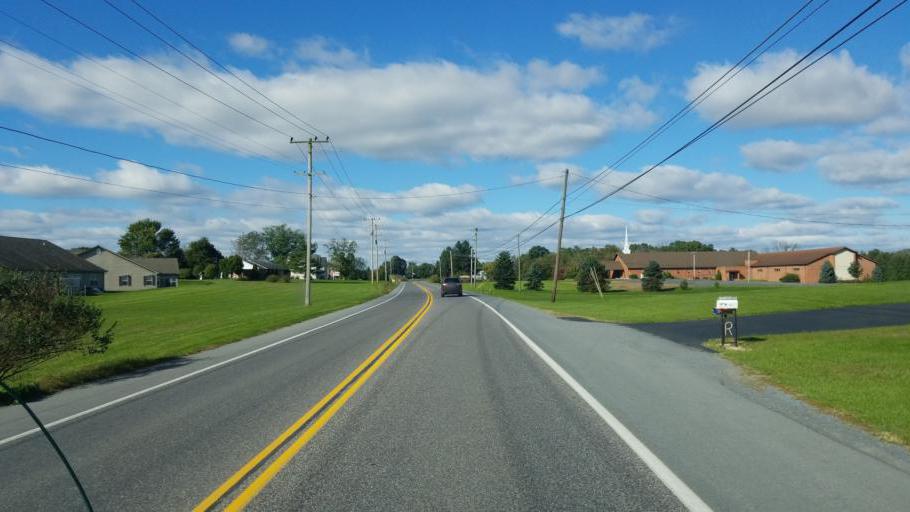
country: US
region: Pennsylvania
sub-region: Franklin County
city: Greencastle
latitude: 39.7997
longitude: -77.7772
